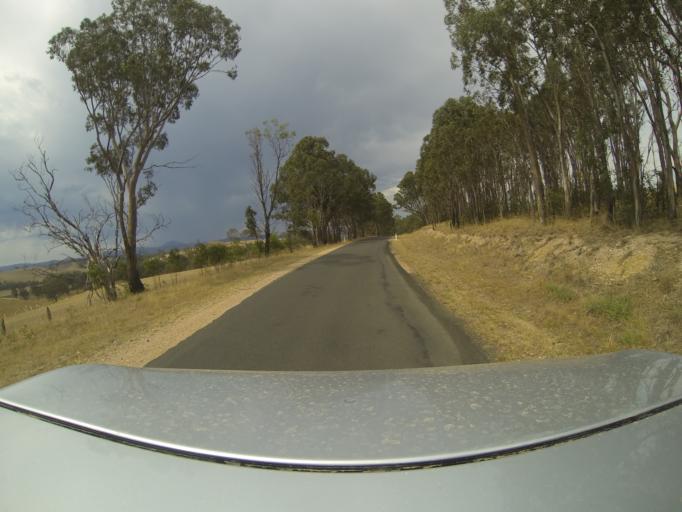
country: AU
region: Victoria
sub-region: Wellington
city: Heyfield
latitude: -37.9011
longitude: 146.7238
